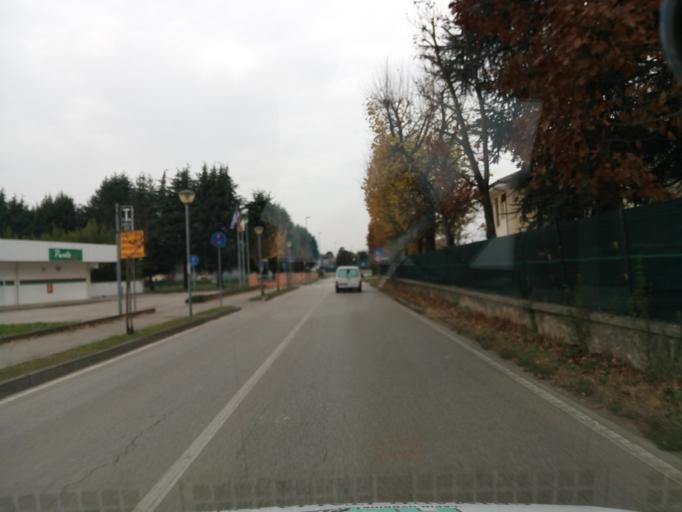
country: IT
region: Veneto
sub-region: Provincia di Treviso
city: Falze
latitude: 45.7413
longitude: 12.0850
